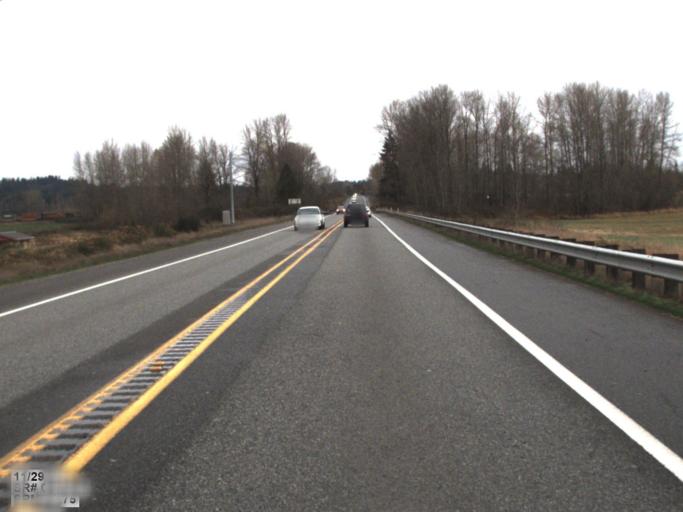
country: US
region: Washington
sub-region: Snohomish County
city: Snohomish
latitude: 47.9036
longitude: -122.1091
